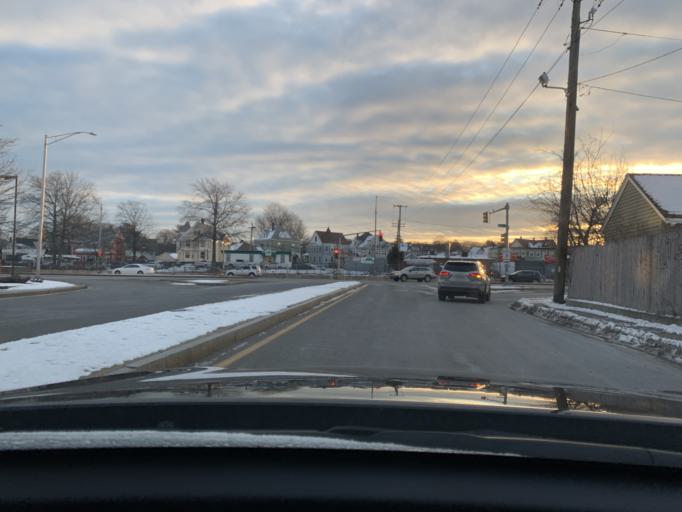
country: US
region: Massachusetts
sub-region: Norfolk County
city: Quincy
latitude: 42.2390
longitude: -71.0065
